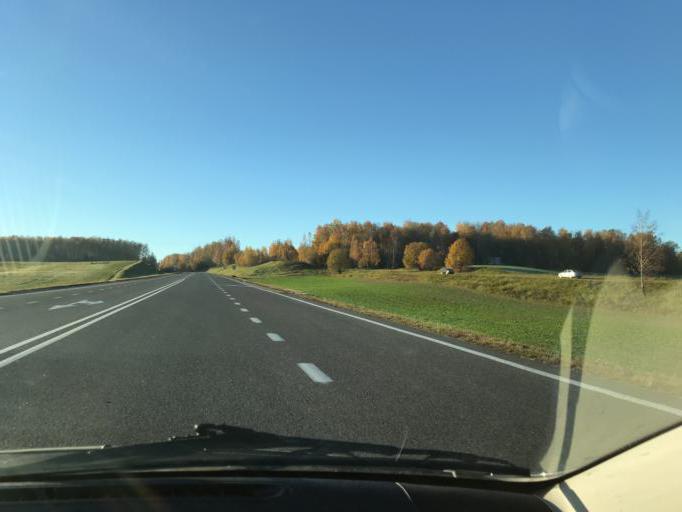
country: BY
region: Vitebsk
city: Vitebsk
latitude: 55.0510
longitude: 30.3127
